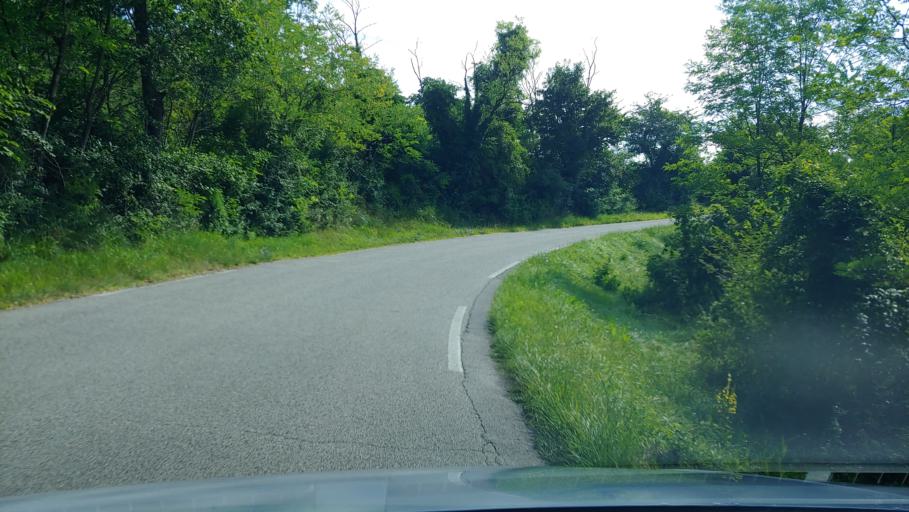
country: SI
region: Komen
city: Komen
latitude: 45.8441
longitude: 13.7750
